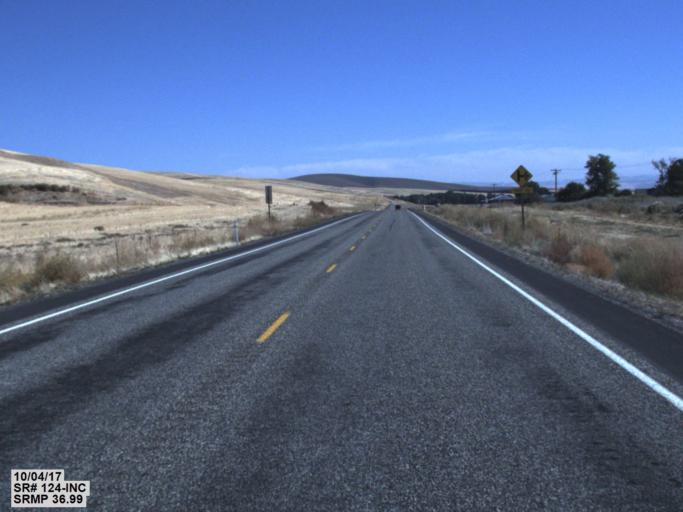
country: US
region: Washington
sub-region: Walla Walla County
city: Waitsburg
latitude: 46.2994
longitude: -118.2967
